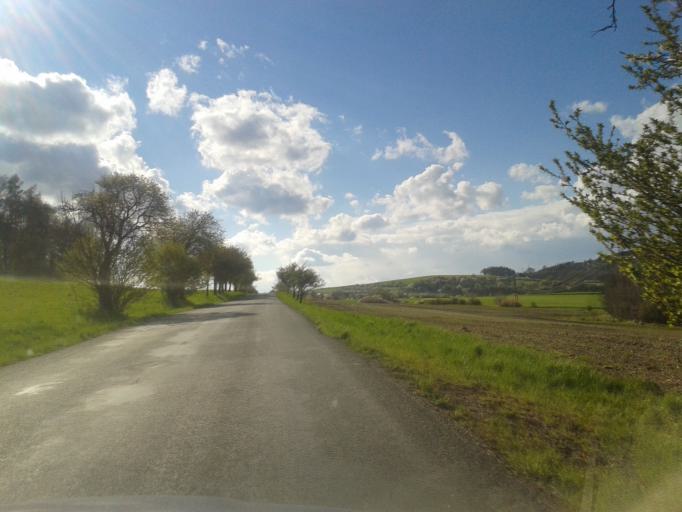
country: CZ
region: Central Bohemia
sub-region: Okres Beroun
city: Lodenice
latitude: 50.0099
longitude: 14.1303
